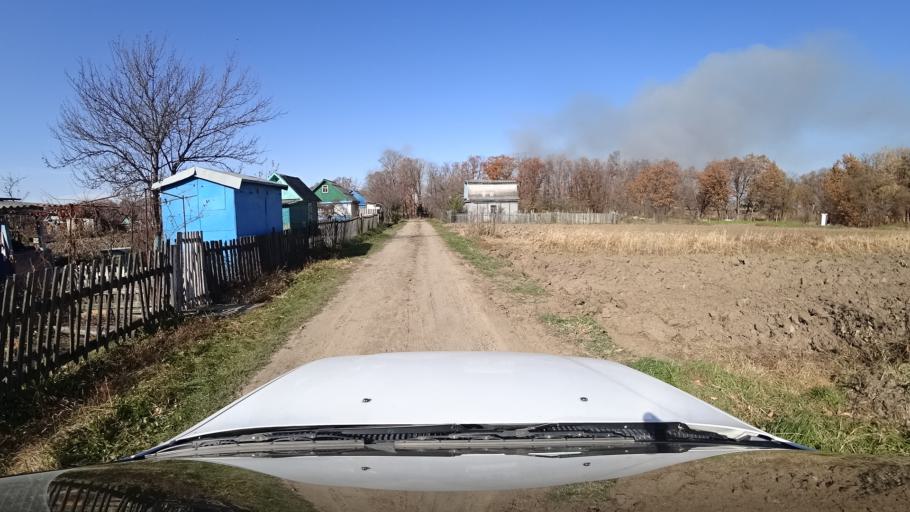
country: RU
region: Primorskiy
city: Dal'nerechensk
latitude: 45.8863
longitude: 133.7461
